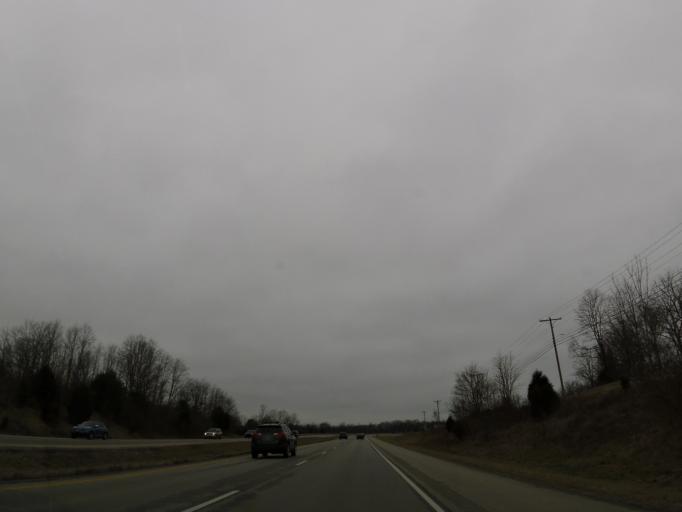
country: US
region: Kentucky
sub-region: Franklin County
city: Frankfort
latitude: 38.1422
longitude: -84.9019
